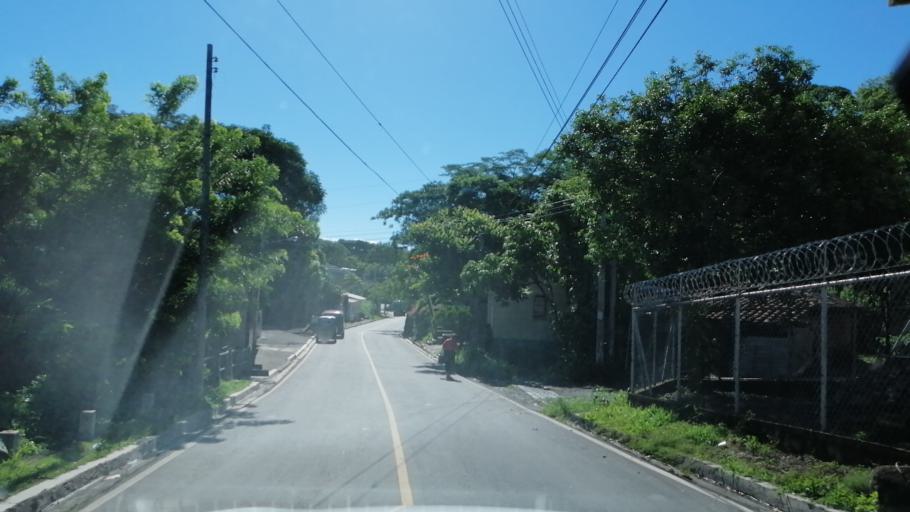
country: SV
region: Morazan
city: Corinto
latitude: 13.8051
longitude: -87.9702
